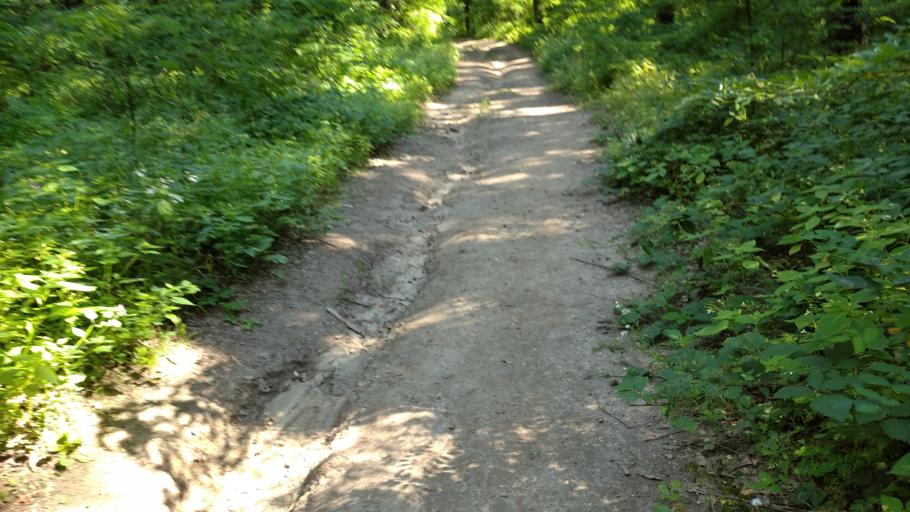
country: HU
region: Nograd
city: Nagyoroszi
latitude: 48.0223
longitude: 19.0388
